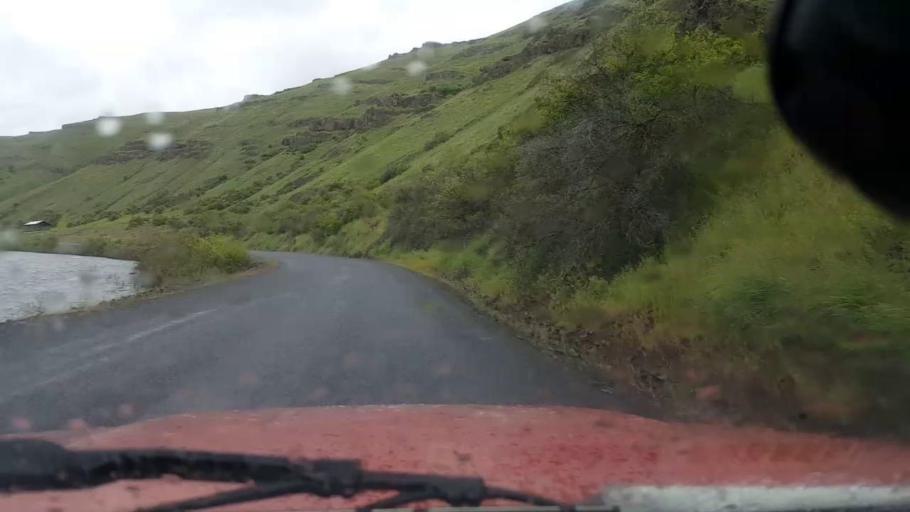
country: US
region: Washington
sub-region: Asotin County
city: Asotin
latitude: 46.0266
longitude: -117.3299
